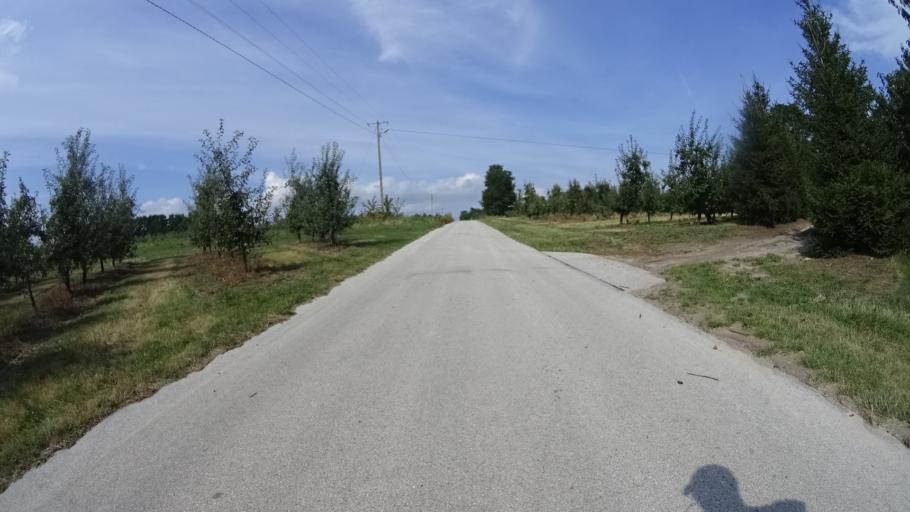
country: PL
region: Masovian Voivodeship
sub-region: Powiat grojecki
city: Goszczyn
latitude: 51.6887
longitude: 20.8443
